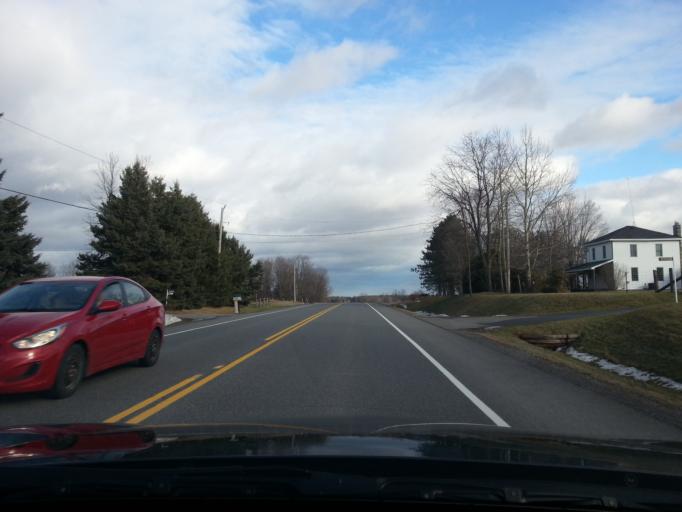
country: CA
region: Ontario
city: Prescott
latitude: 45.0528
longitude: -75.5407
